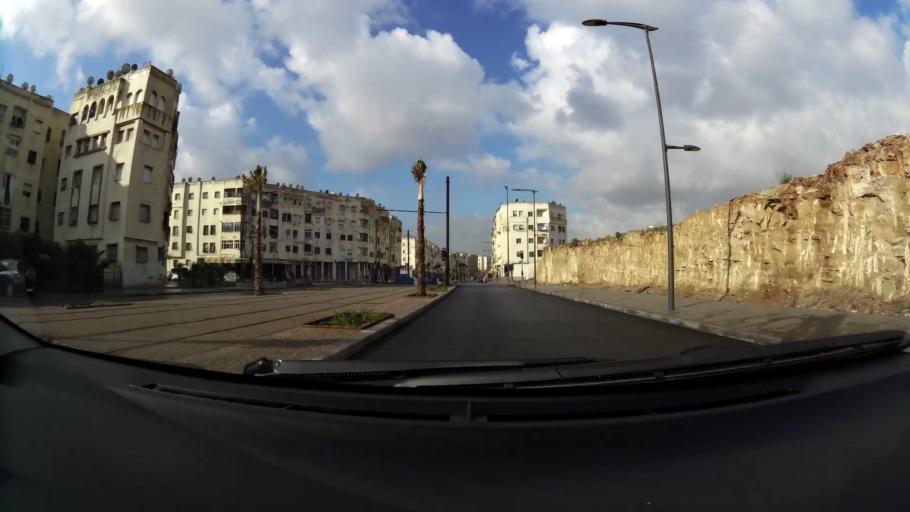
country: MA
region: Grand Casablanca
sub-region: Mediouna
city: Tit Mellil
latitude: 33.5978
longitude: -7.5354
